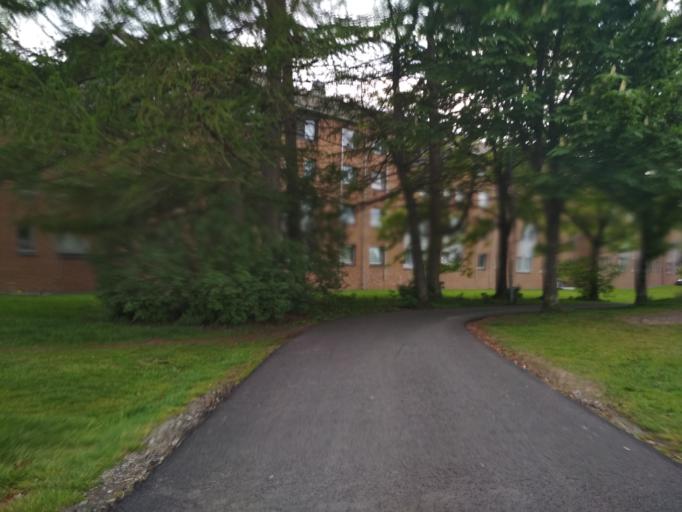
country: NO
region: Rogaland
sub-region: Stavanger
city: Stavanger
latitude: 58.9498
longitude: 5.7197
